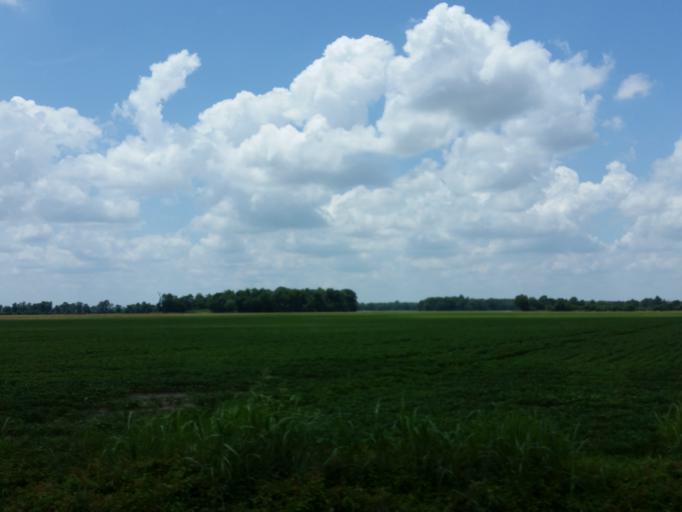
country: US
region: Tennessee
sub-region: Lake County
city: Ridgely
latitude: 36.1769
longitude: -89.4453
